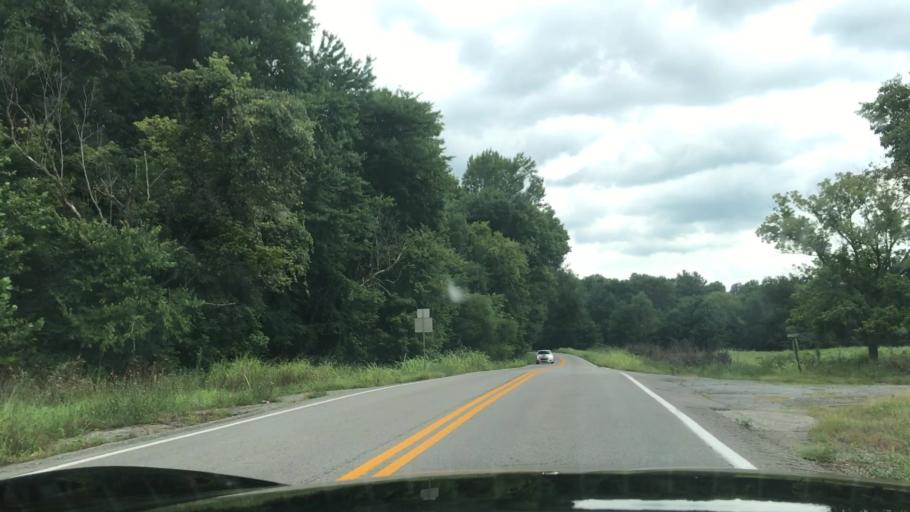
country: US
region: Kentucky
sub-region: Muhlenberg County
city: Central City
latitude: 37.1973
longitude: -87.0353
